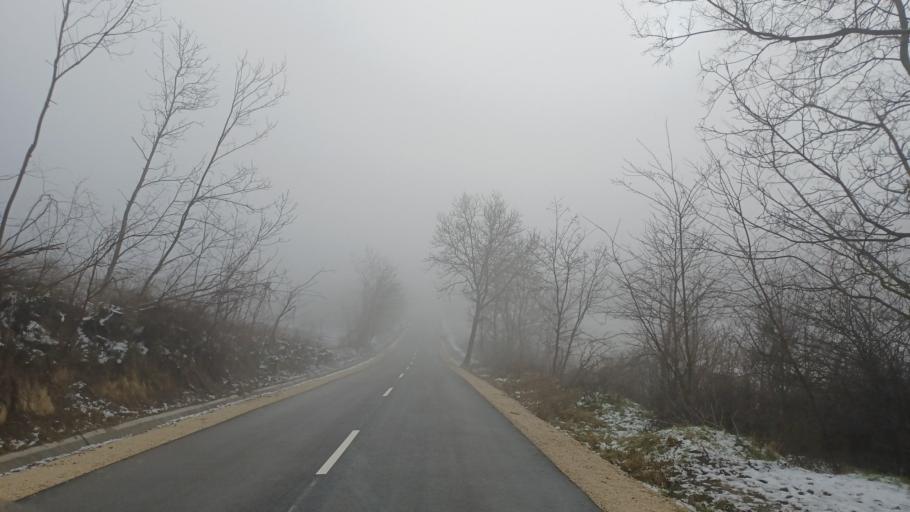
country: HU
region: Tolna
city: Gyonk
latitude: 46.5838
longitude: 18.4737
